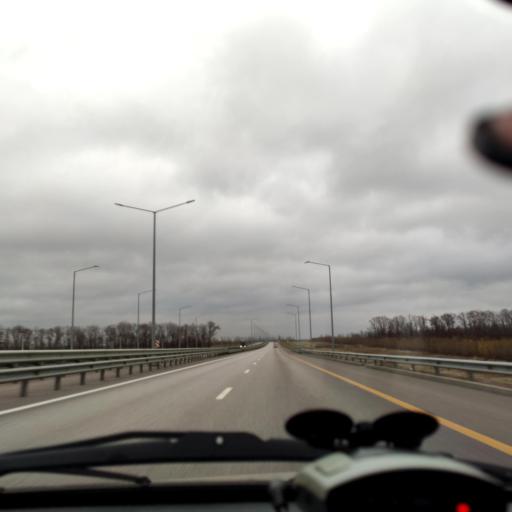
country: RU
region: Voronezj
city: Podkletnoye
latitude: 51.5886
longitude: 39.4207
